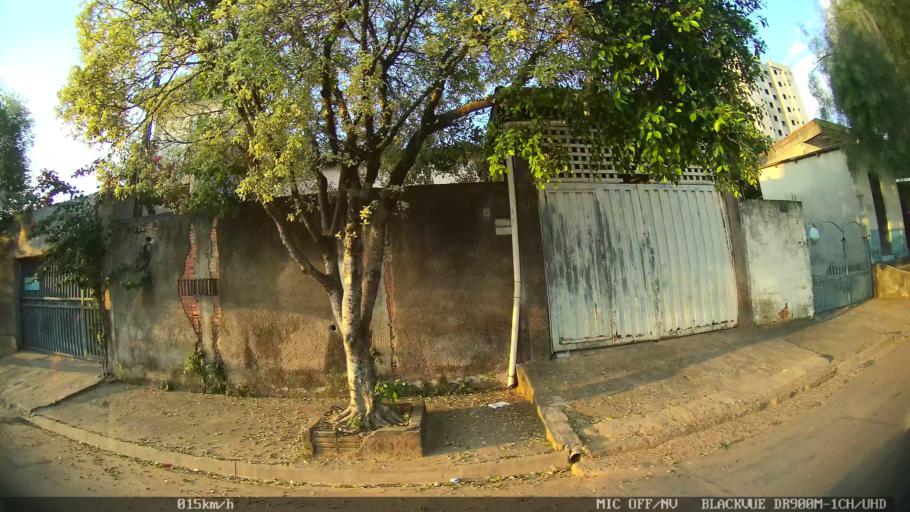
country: BR
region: Sao Paulo
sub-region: Hortolandia
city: Hortolandia
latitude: -22.8624
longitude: -47.2065
